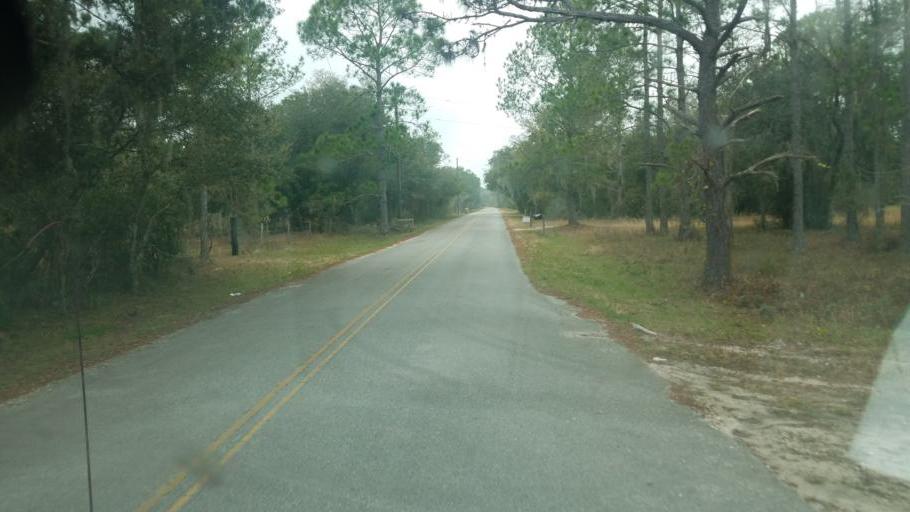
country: US
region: Florida
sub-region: Lake County
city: Groveland
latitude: 28.3875
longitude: -81.8511
